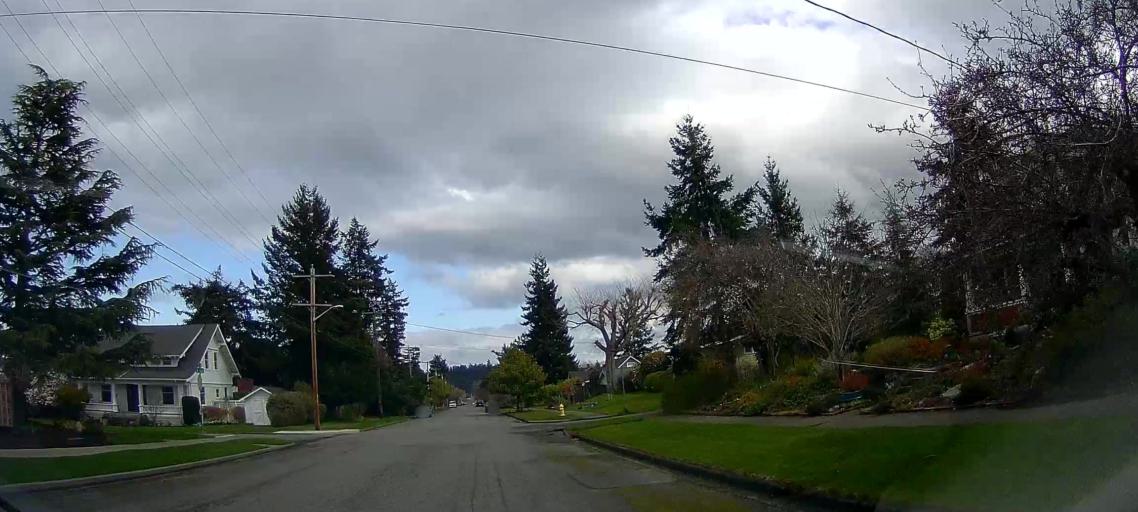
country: US
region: Washington
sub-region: Skagit County
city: Anacortes
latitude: 48.5151
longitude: -122.6256
